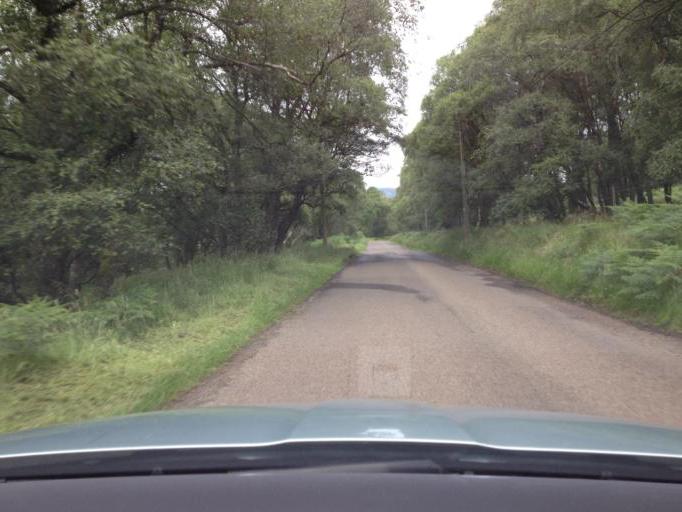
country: GB
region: Scotland
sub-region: Angus
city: Brechin
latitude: 56.8706
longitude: -2.7014
